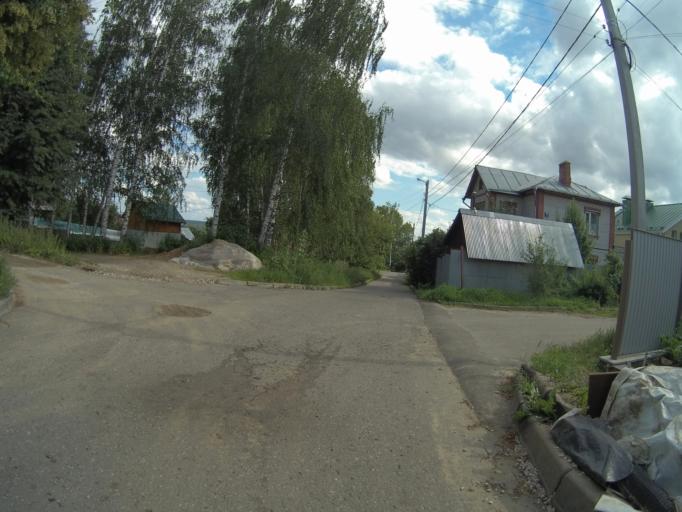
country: RU
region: Vladimir
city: Vladimir
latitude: 56.1173
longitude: 40.3817
